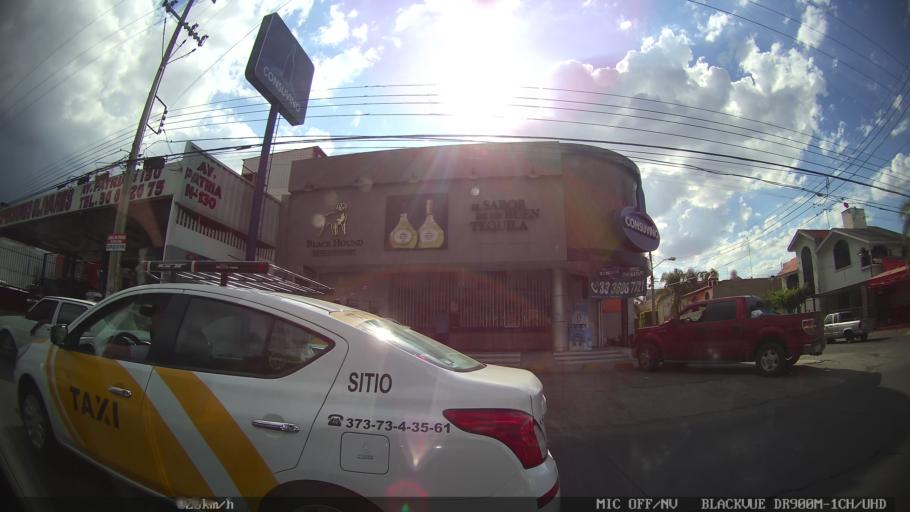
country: MX
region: Jalisco
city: Tlaquepaque
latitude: 20.6356
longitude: -103.2842
